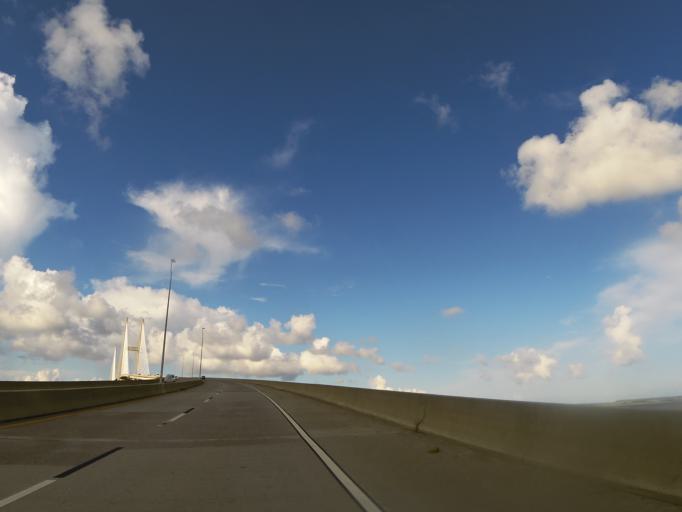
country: US
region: Georgia
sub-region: Glynn County
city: Brunswick
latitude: 31.1083
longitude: -81.4895
